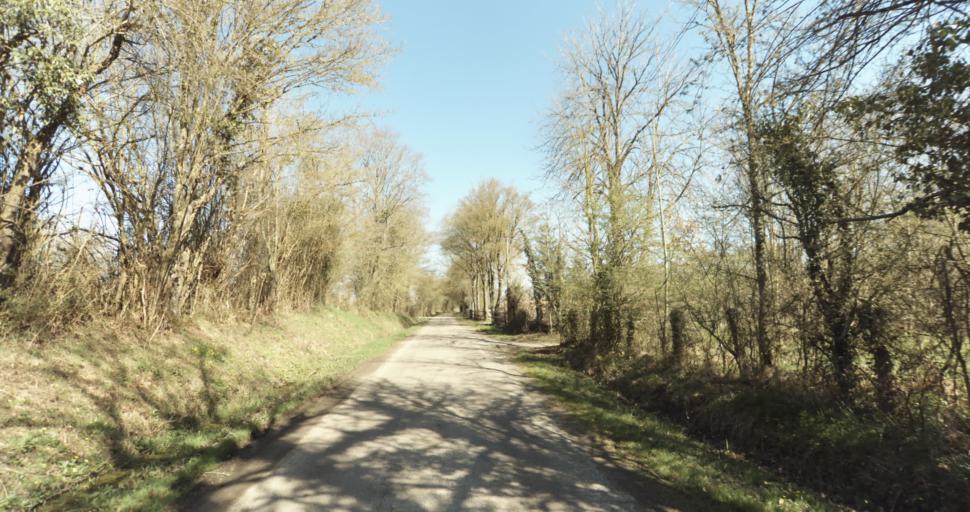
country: FR
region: Lower Normandy
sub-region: Departement du Calvados
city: Livarot
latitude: 49.0061
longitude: 0.0731
